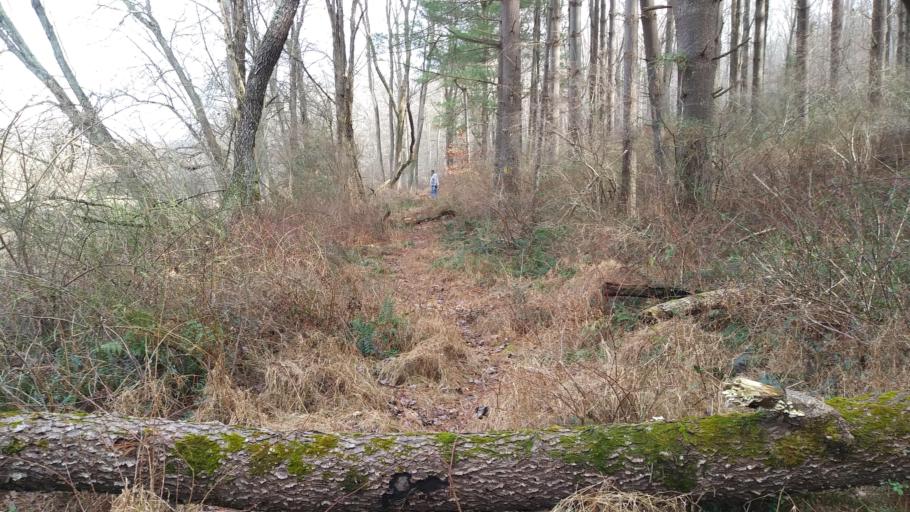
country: US
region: Pennsylvania
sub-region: York County
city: Susquehanna Trails
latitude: 39.6840
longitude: -76.2748
